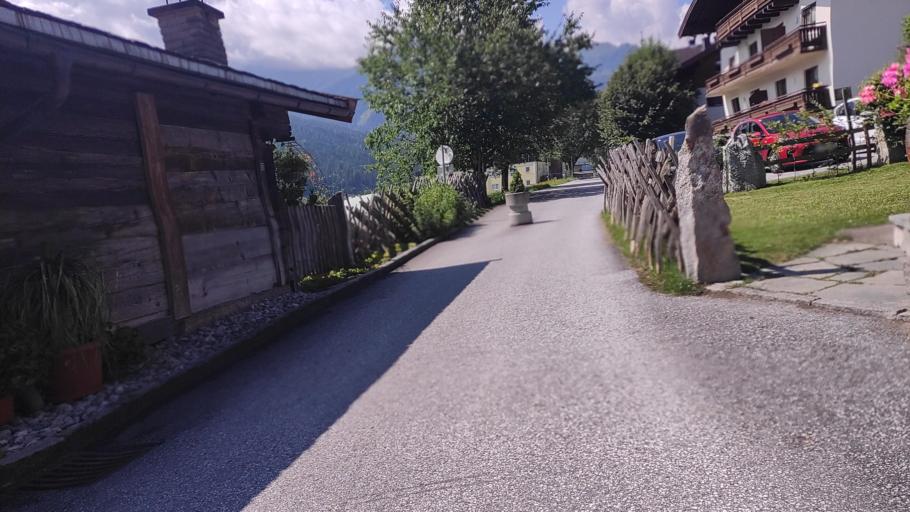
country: AT
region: Salzburg
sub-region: Politischer Bezirk Zell am See
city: Bramberg am Wildkogel
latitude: 47.2701
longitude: 12.3387
